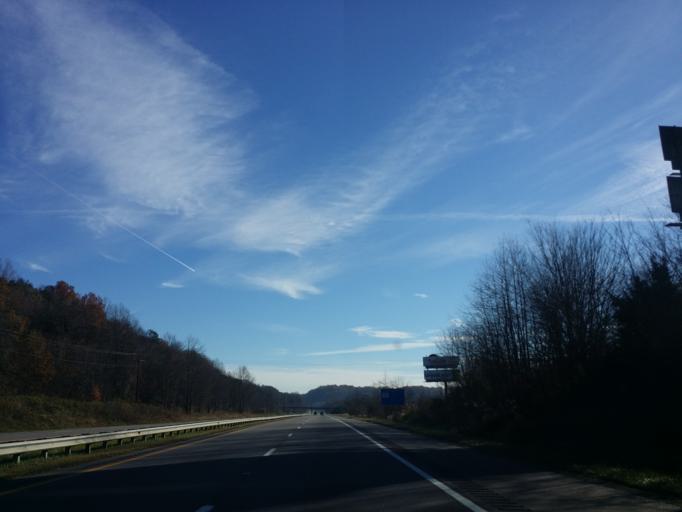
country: US
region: North Carolina
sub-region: McDowell County
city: West Marion
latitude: 35.6386
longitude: -82.1521
